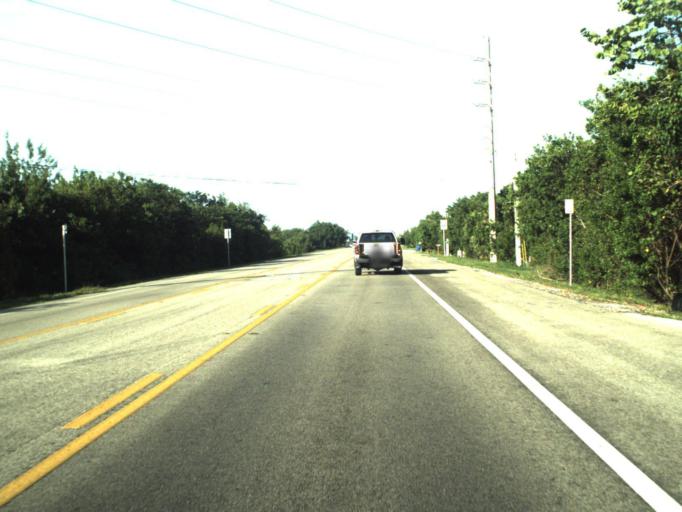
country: US
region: Florida
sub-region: Monroe County
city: Marathon
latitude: 24.7614
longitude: -80.9523
